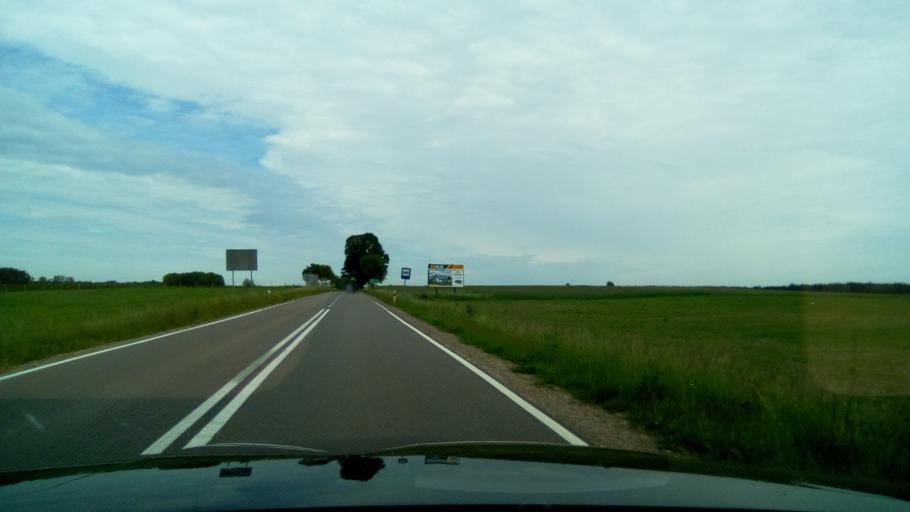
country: PL
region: Pomeranian Voivodeship
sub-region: Powiat czluchowski
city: Przechlewo
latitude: 53.8209
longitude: 17.4064
